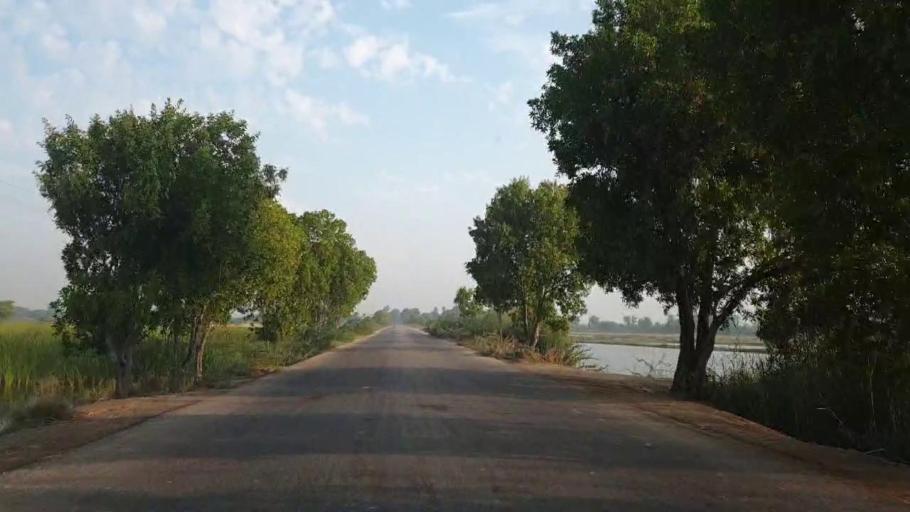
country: PK
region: Sindh
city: Tando Bago
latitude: 24.7369
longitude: 68.9458
